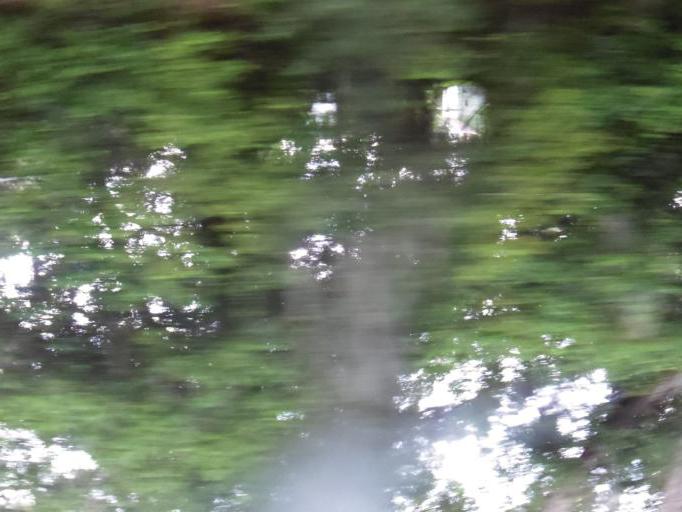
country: US
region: Florida
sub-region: Duval County
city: Jacksonville
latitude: 30.3448
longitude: -81.6081
